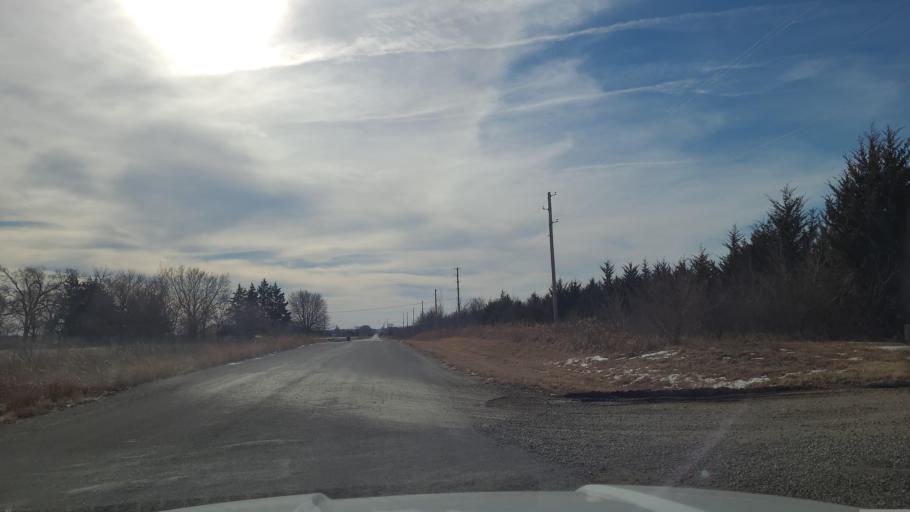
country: US
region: Kansas
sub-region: Douglas County
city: Lawrence
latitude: 38.9030
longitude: -95.2052
